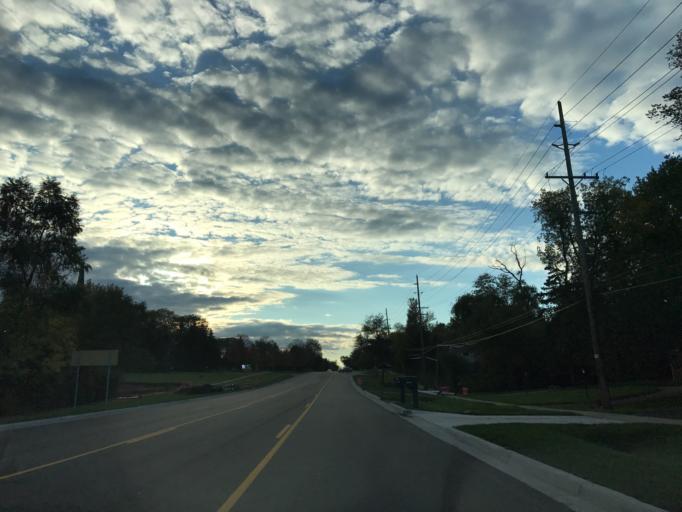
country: US
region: Michigan
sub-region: Oakland County
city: Farmington Hills
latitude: 42.4852
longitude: -83.3399
